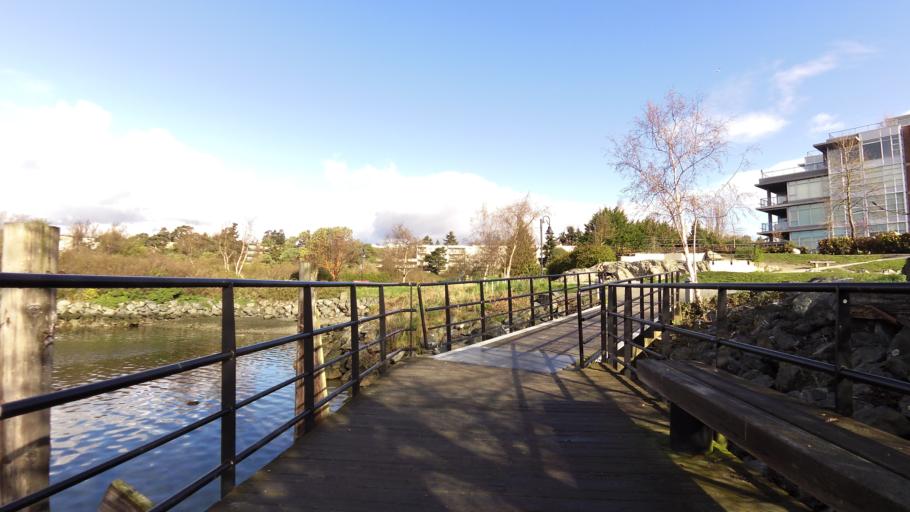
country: CA
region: British Columbia
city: Victoria
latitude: 48.4409
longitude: -123.3801
